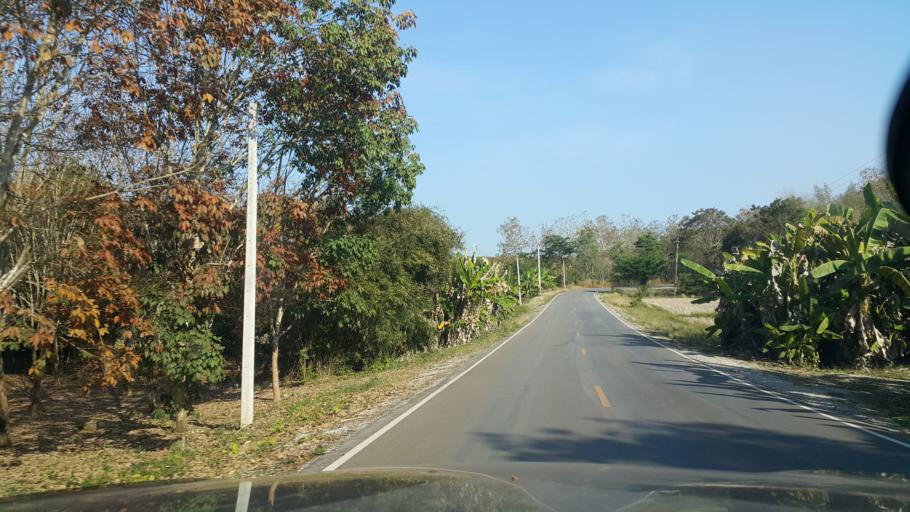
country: TH
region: Loei
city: Chiang Khan
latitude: 17.8246
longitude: 101.6272
